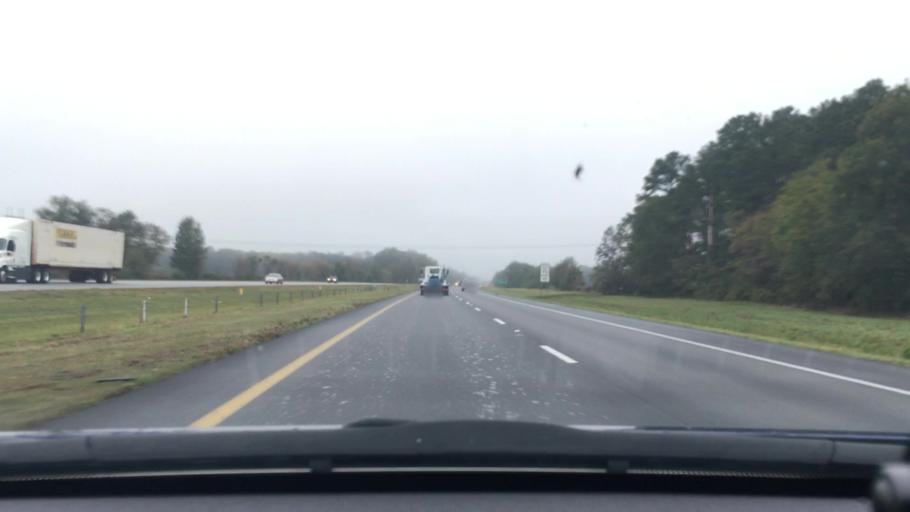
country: US
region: South Carolina
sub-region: Lee County
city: Bishopville
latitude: 34.1865
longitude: -80.2238
